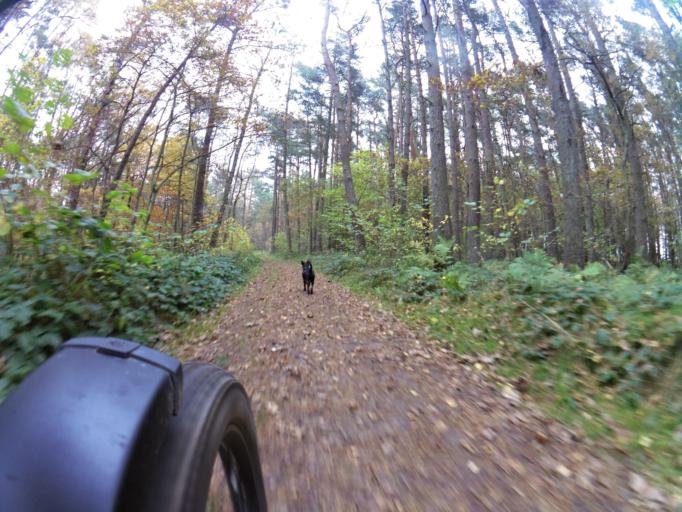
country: PL
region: Pomeranian Voivodeship
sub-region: Powiat pucki
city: Krokowa
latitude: 54.8295
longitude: 18.1245
